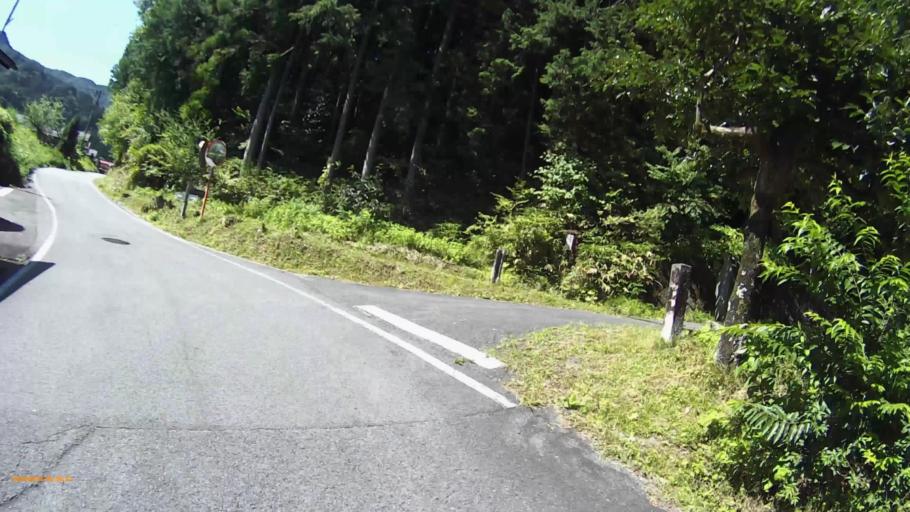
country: JP
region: Nagano
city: Iida
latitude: 35.6838
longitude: 137.6740
